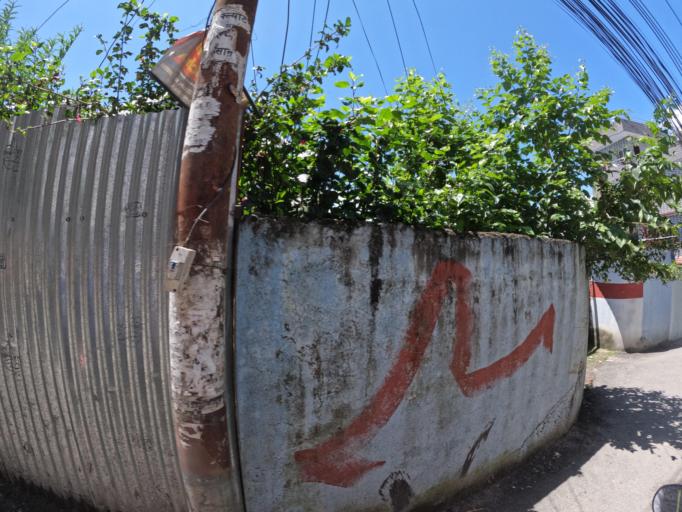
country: NP
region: Central Region
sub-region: Bagmati Zone
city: Kathmandu
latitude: 27.7488
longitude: 85.3273
